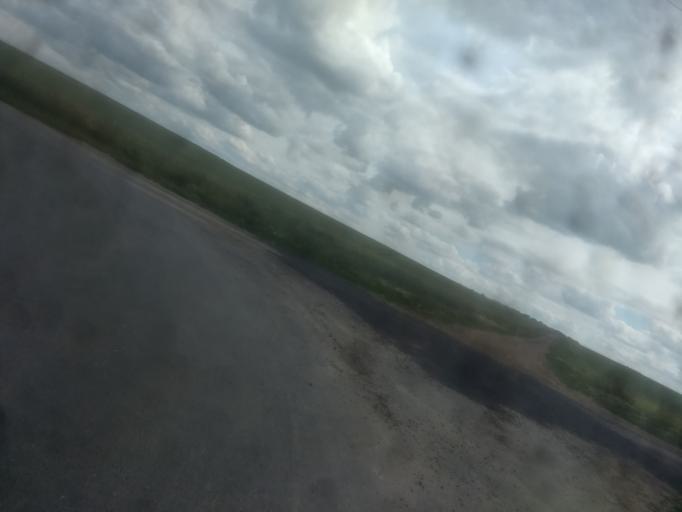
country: FR
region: Nord-Pas-de-Calais
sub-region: Departement du Pas-de-Calais
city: Duisans
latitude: 50.2915
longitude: 2.6919
